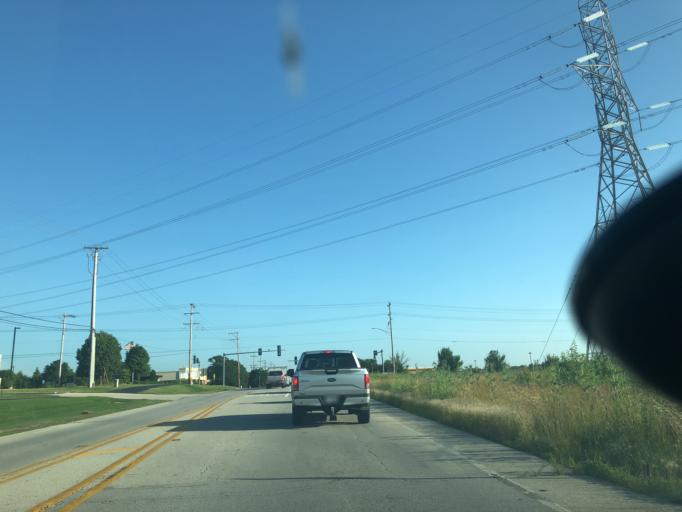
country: US
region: Illinois
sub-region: Will County
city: Mokena
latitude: 41.5654
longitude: -87.8905
